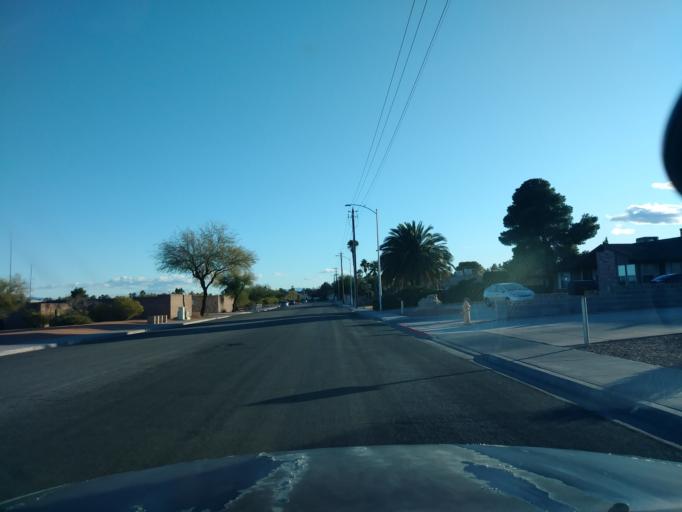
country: US
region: Nevada
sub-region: Clark County
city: Spring Valley
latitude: 36.1509
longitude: -115.2388
